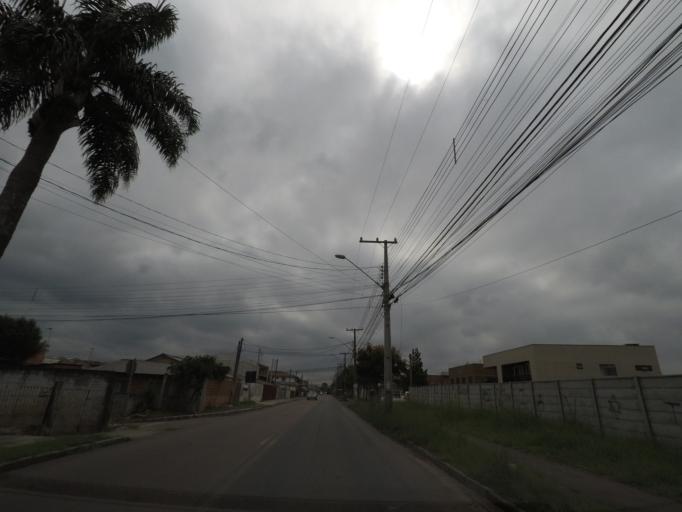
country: BR
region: Parana
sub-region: Curitiba
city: Curitiba
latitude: -25.5070
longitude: -49.3346
